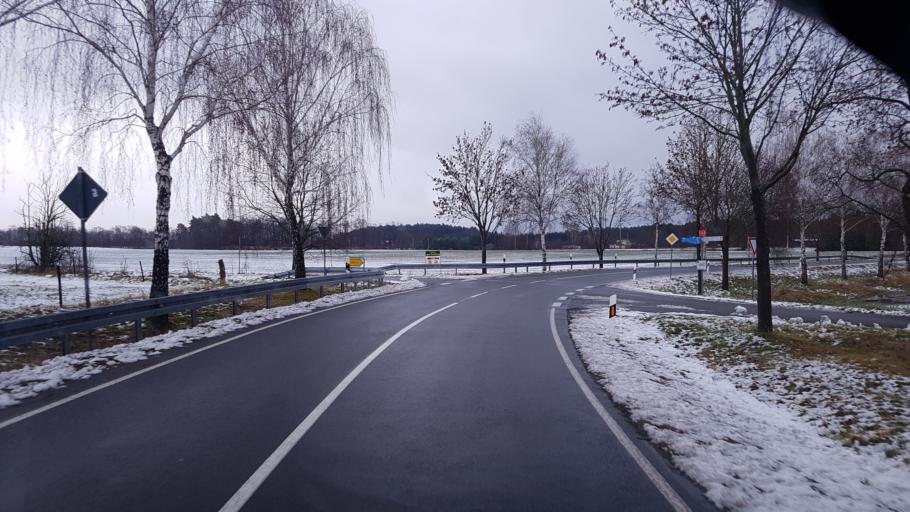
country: DE
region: Brandenburg
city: Schenkendobern
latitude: 51.9132
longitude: 14.6258
